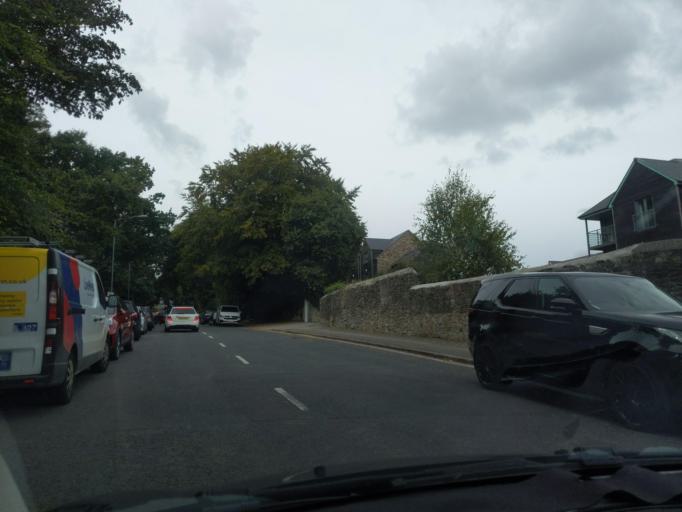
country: GB
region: England
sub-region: Cornwall
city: St Austell
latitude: 50.3364
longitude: -4.7635
